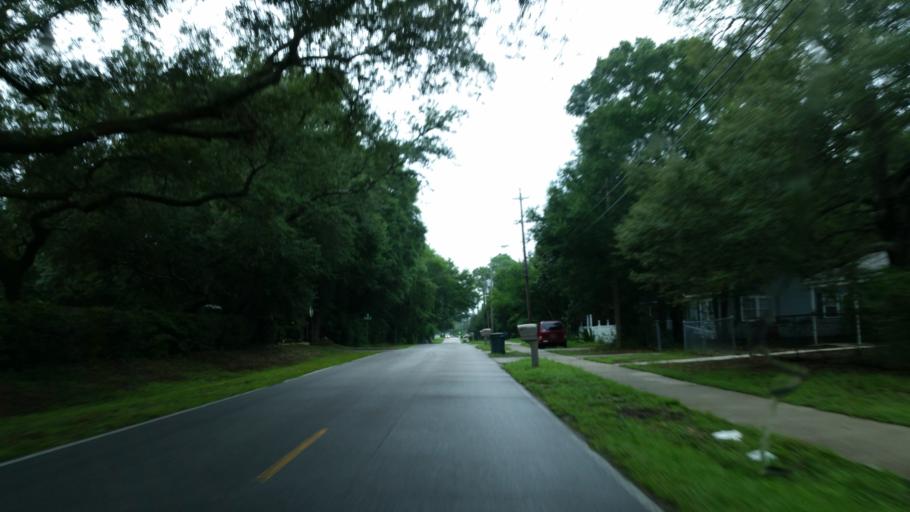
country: US
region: Florida
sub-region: Escambia County
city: Warrington
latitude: 30.3864
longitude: -87.2852
